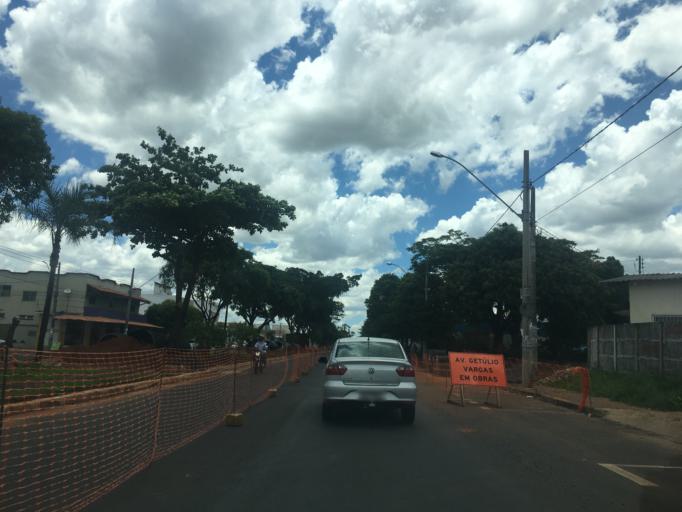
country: BR
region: Minas Gerais
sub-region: Uberlandia
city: Uberlandia
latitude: -18.9428
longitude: -48.3098
